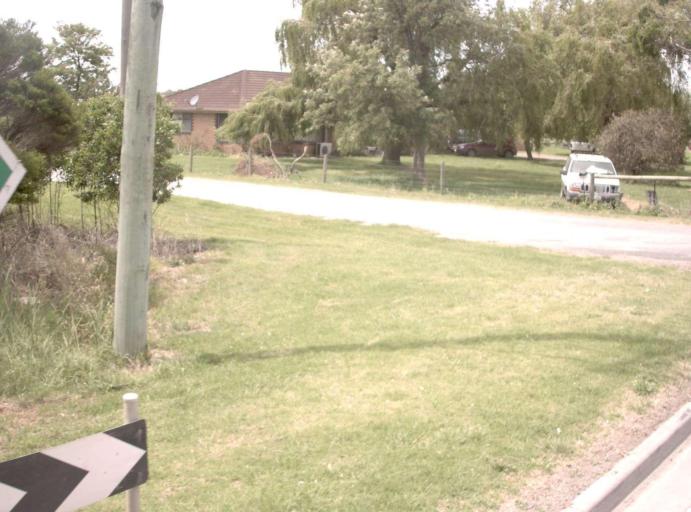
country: AU
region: Victoria
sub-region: Mornington Peninsula
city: Tyabb
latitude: -38.2240
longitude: 145.2177
